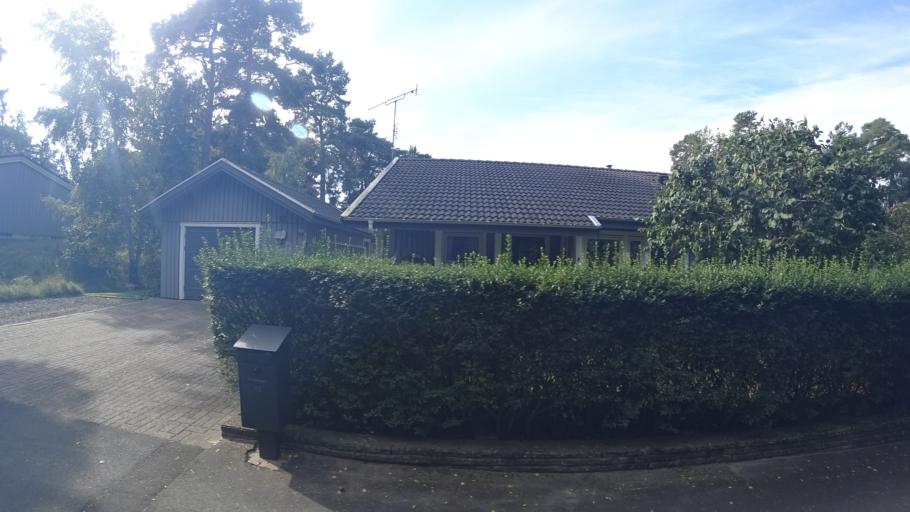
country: SE
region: Skane
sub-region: Kristianstads Kommun
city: Ahus
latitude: 55.9178
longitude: 14.2970
